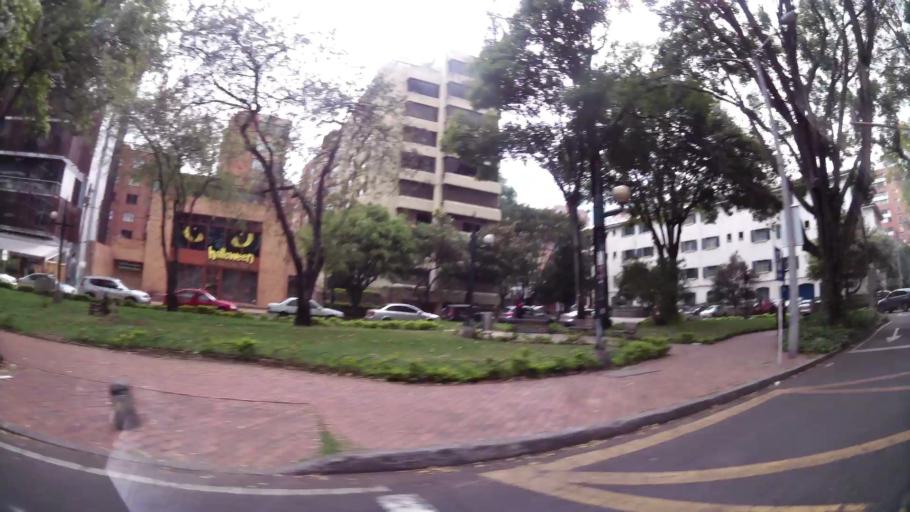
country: CO
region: Bogota D.C.
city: Barrio San Luis
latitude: 4.6653
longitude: -74.0506
